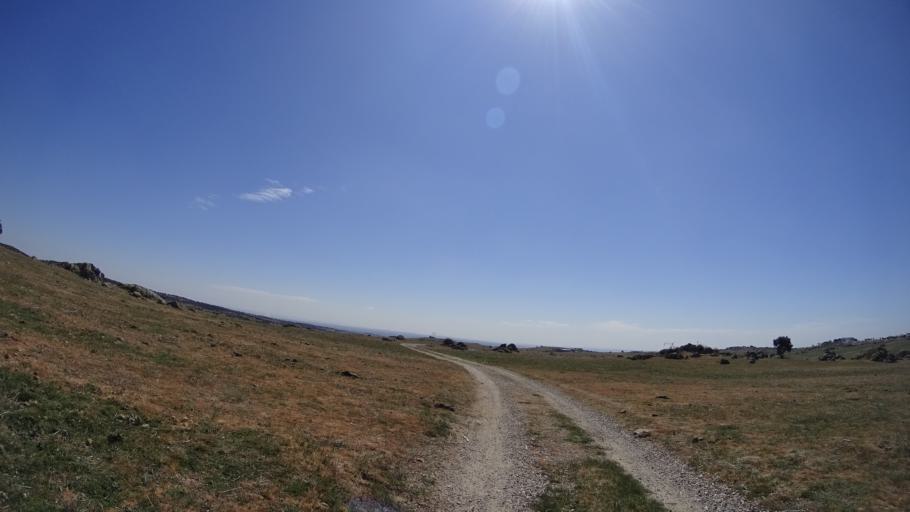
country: ES
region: Madrid
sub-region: Provincia de Madrid
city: Colmenar Viejo
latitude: 40.7034
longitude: -3.7520
